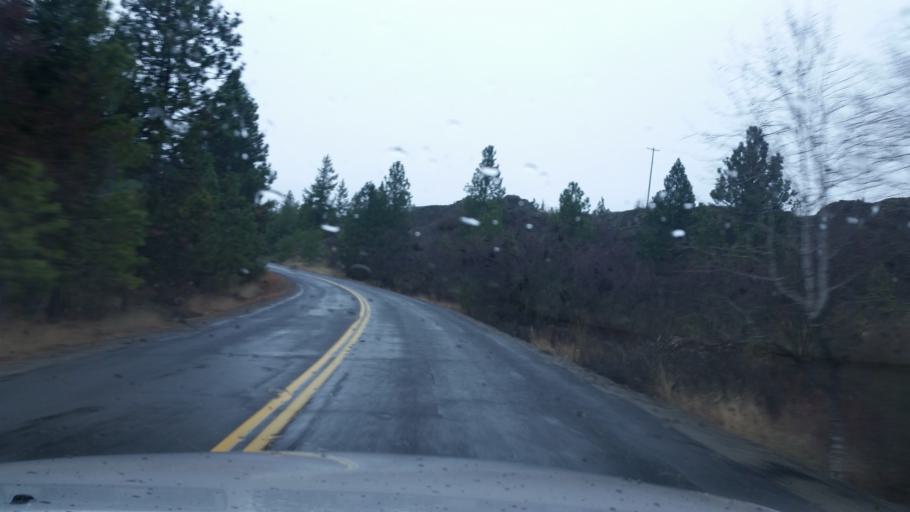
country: US
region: Washington
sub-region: Spokane County
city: Airway Heights
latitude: 47.6975
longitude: -117.5722
